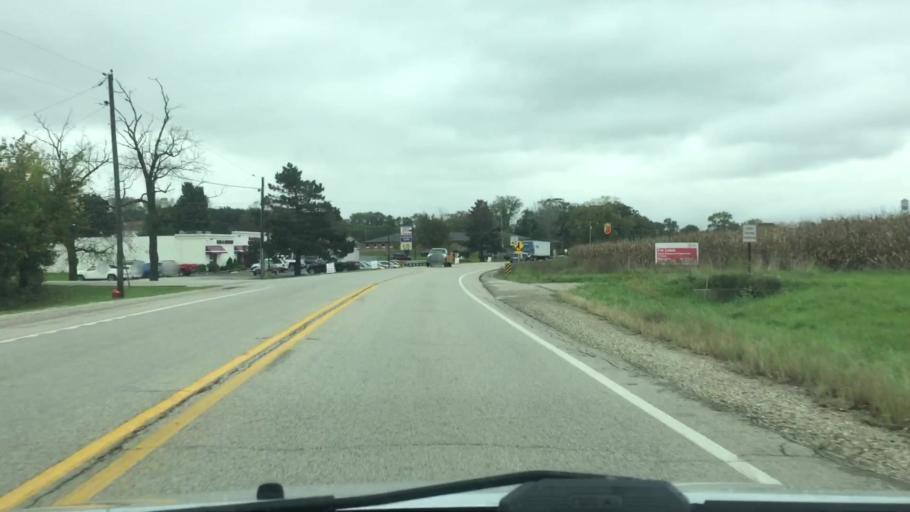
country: US
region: Illinois
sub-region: McHenry County
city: Richmond
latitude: 42.4909
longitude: -88.3075
